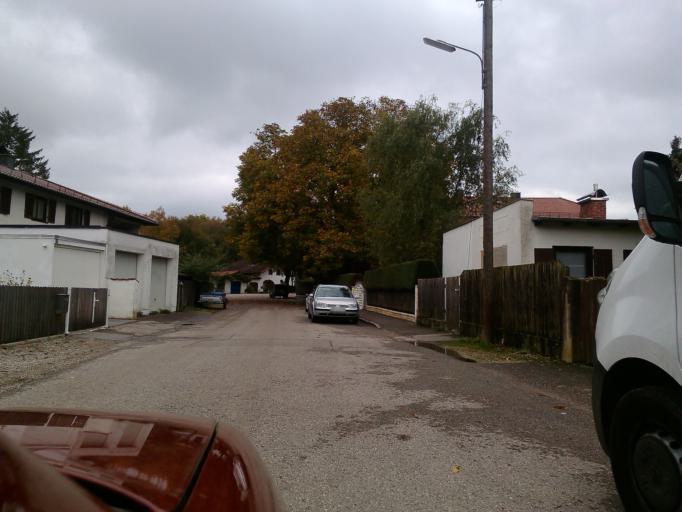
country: DE
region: Bavaria
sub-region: Upper Bavaria
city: Gauting
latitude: 48.0623
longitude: 11.3774
